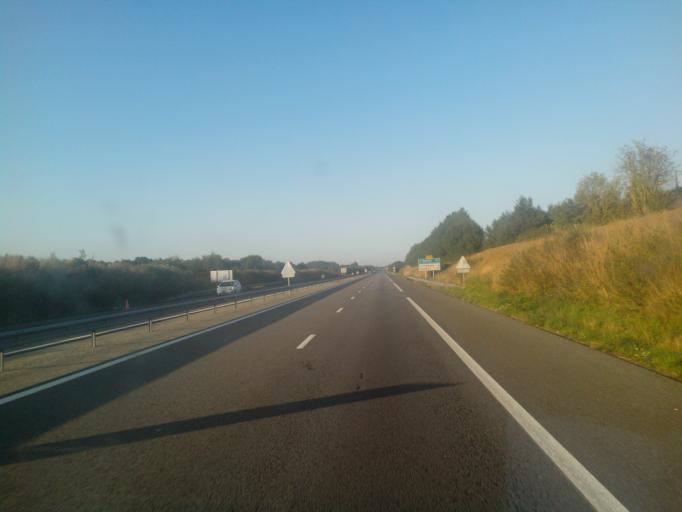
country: FR
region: Brittany
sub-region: Departement du Morbihan
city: Noyal-Pontivy
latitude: 48.1105
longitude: -2.8700
